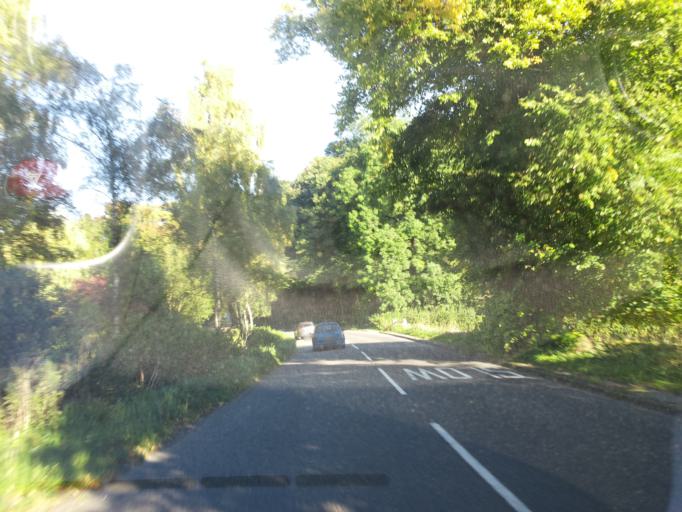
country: GB
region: England
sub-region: Derbyshire
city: Bakewell
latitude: 53.2336
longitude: -1.6896
